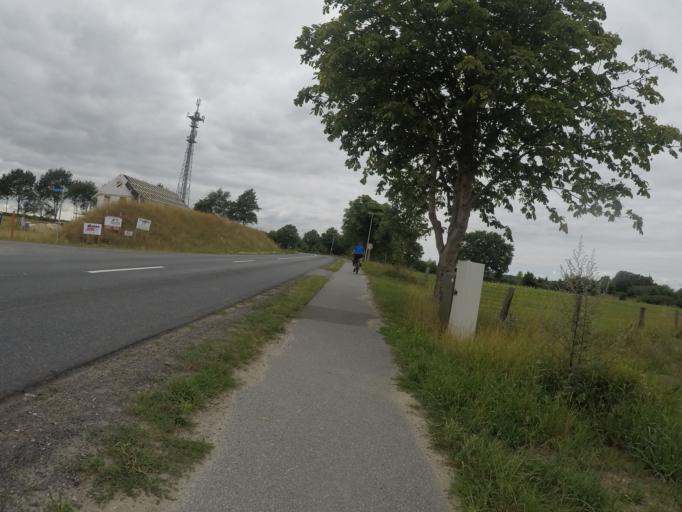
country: DE
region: Lower Saxony
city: Hemmoor
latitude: 53.6926
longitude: 9.1420
